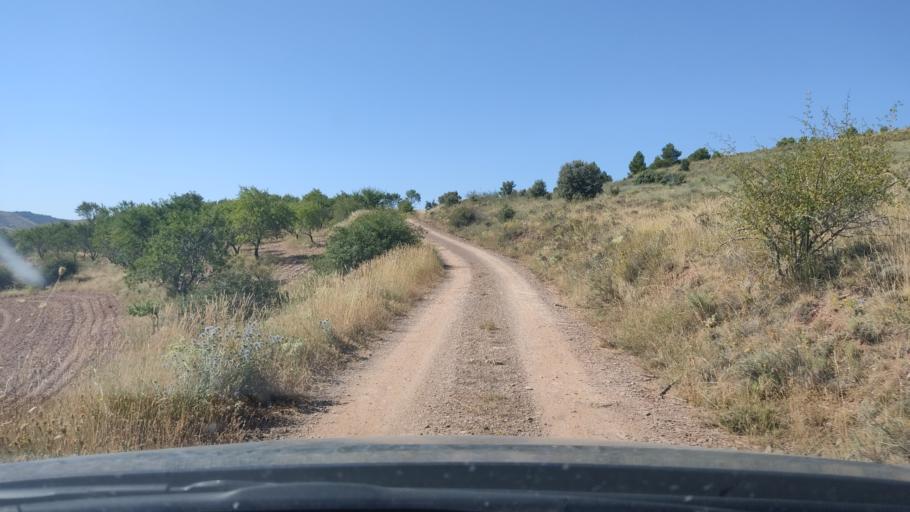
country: ES
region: Aragon
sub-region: Provincia de Teruel
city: Monforte de Moyuela
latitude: 41.0460
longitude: -1.0336
